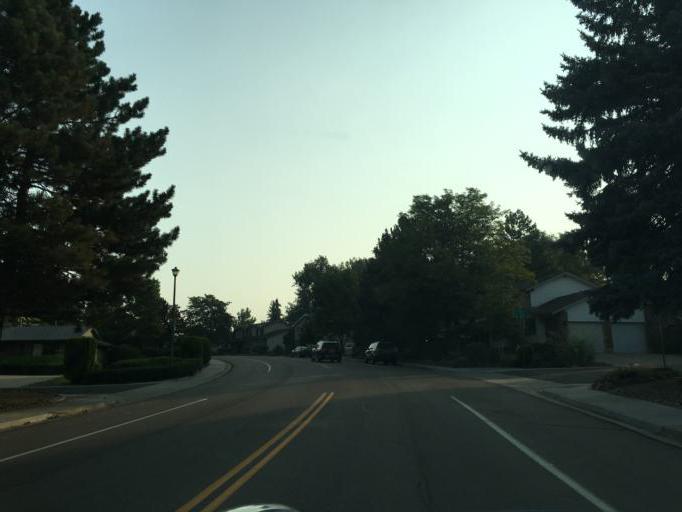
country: US
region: Colorado
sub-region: Adams County
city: Westminster
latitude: 39.8794
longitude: -105.0479
